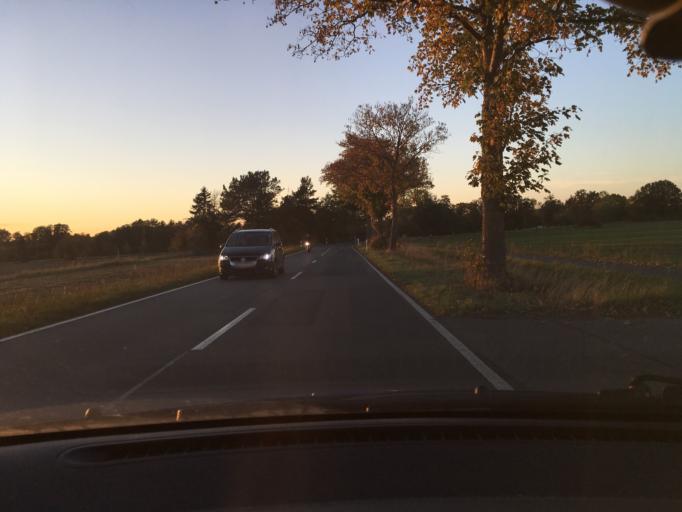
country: DE
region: Lower Saxony
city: Bleckede
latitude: 53.3092
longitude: 10.6813
